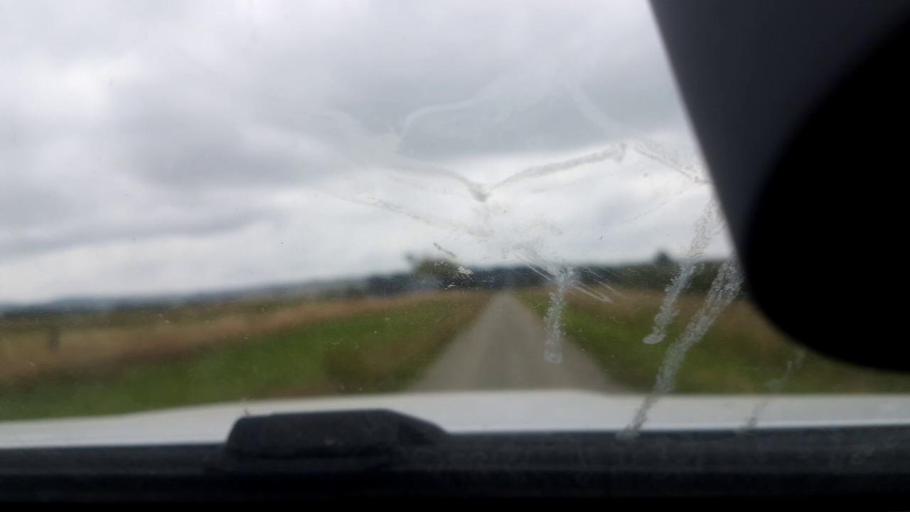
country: NZ
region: Canterbury
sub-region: Timaru District
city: Pleasant Point
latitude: -44.2277
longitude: 171.1653
